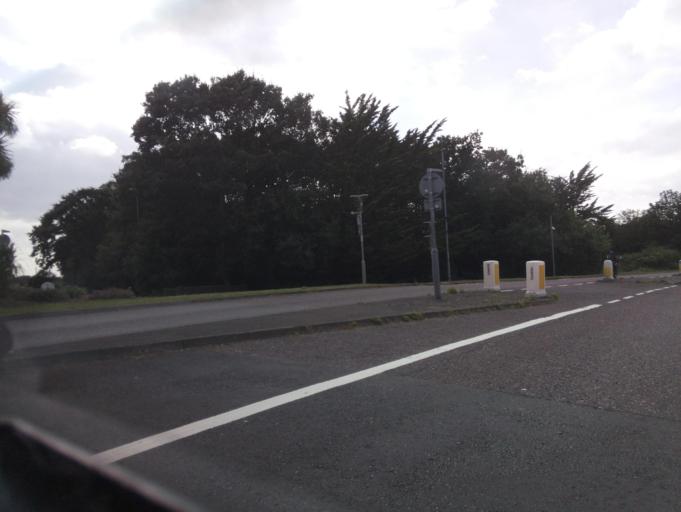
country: GB
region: England
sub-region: Hampshire
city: Bransgore
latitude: 50.7397
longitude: -1.7285
